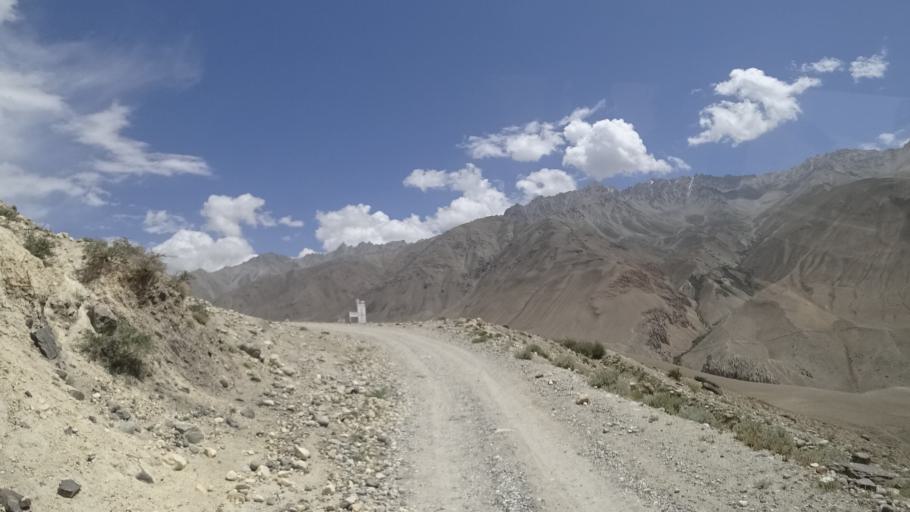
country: AF
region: Badakhshan
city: Khandud
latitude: 37.0831
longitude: 72.6984
